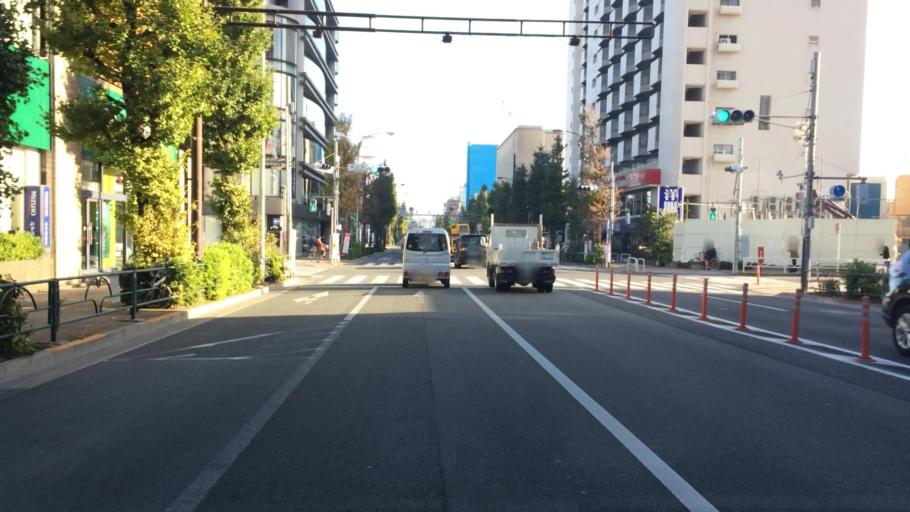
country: JP
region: Tokyo
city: Tokyo
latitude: 35.6228
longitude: 139.6842
